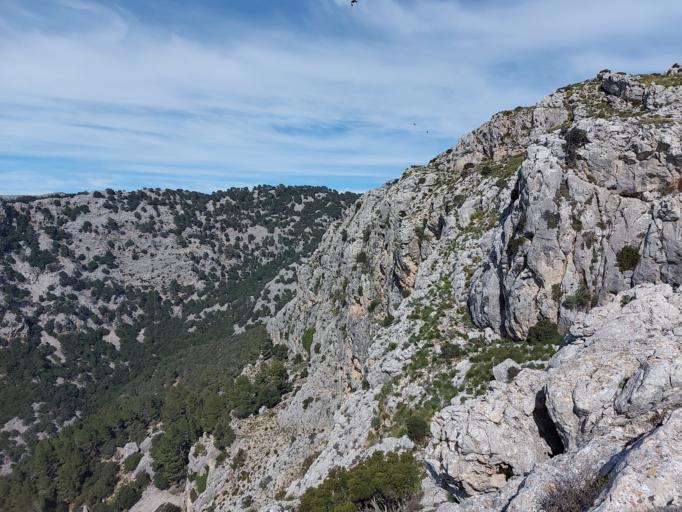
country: ES
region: Balearic Islands
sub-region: Illes Balears
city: Valldemossa
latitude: 39.7125
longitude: 2.6577
